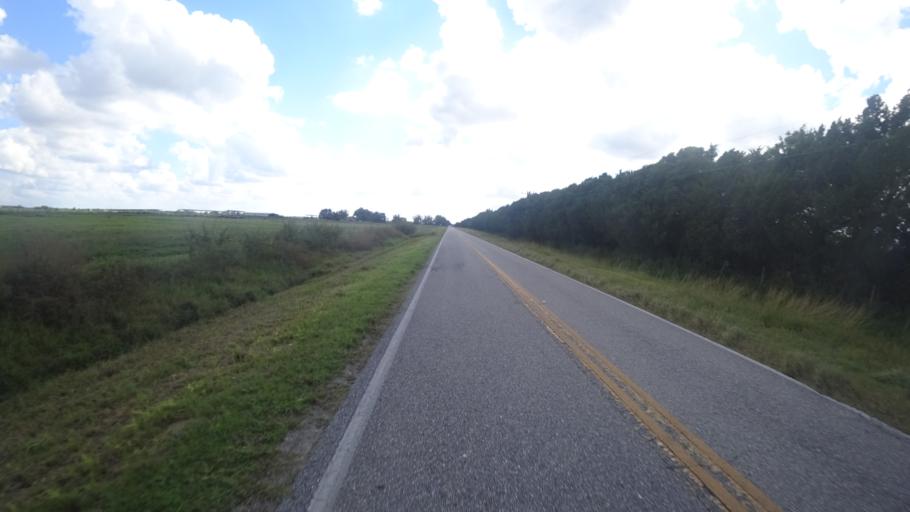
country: US
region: Florida
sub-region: DeSoto County
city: Arcadia
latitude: 27.2950
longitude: -82.1134
